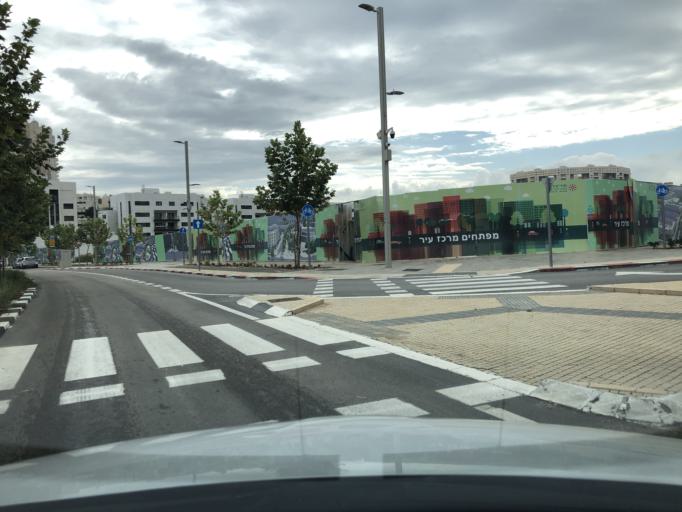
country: IL
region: Central District
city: Modiin
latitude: 31.9032
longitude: 35.0077
